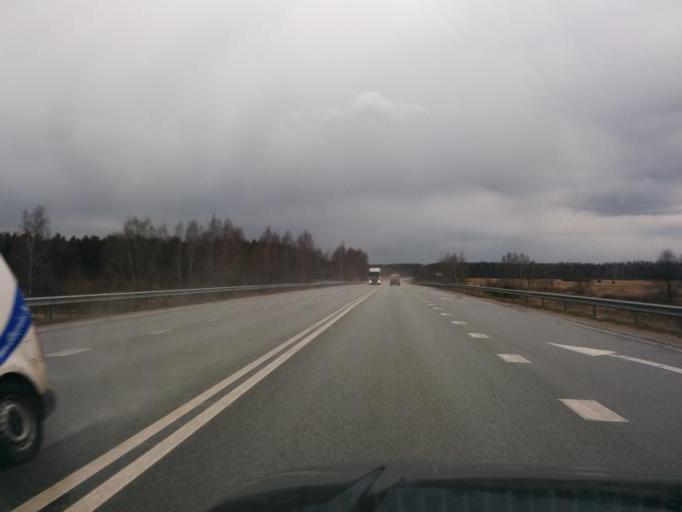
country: LV
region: Marupe
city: Marupe
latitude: 56.8356
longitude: 24.0358
